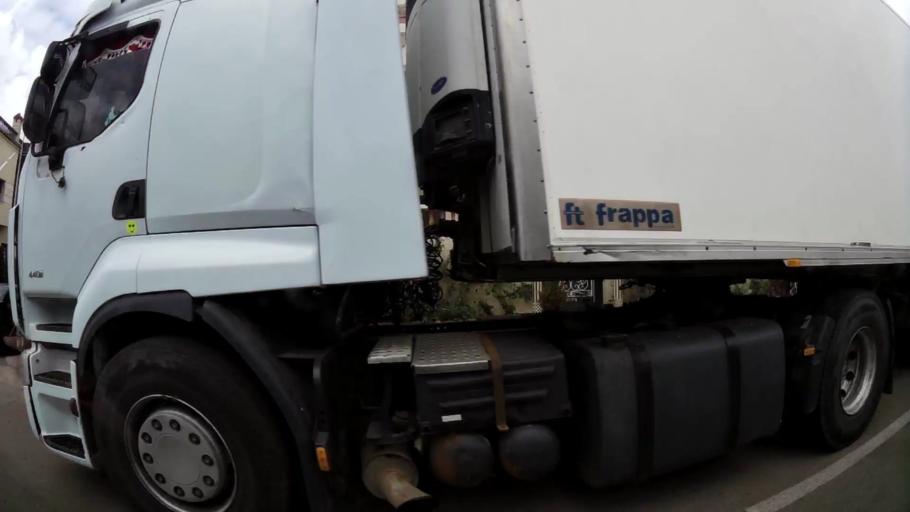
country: MA
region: Grand Casablanca
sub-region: Casablanca
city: Casablanca
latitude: 33.5315
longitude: -7.5883
